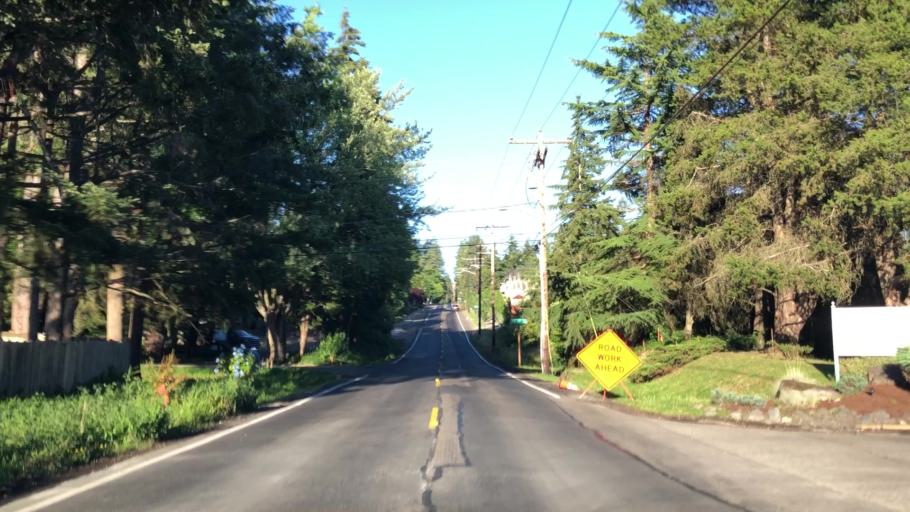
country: US
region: Washington
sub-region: Snohomish County
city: North Creek
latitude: 47.8202
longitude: -122.2035
